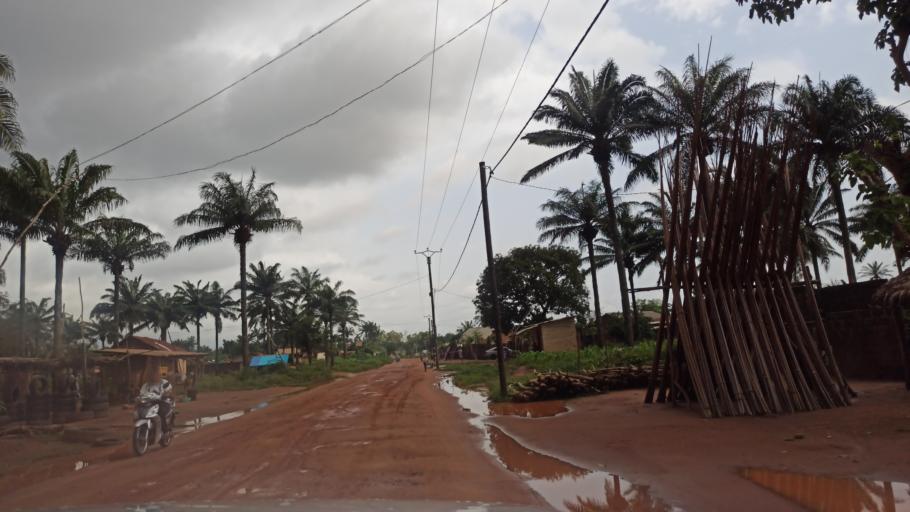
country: BJ
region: Queme
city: Porto-Novo
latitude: 6.5582
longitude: 2.5923
